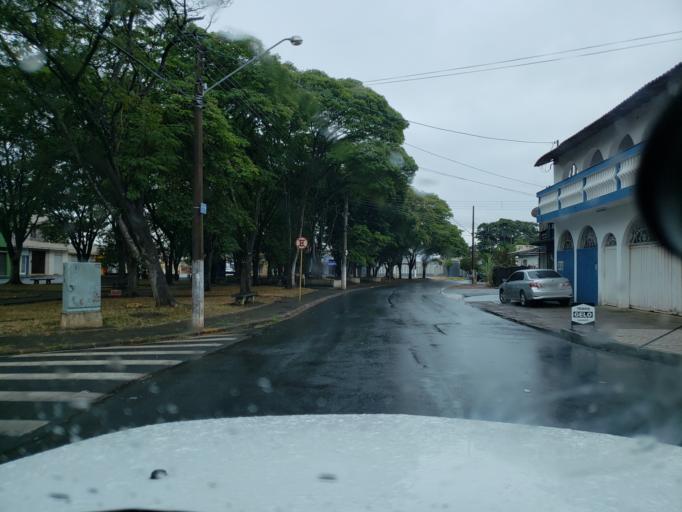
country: BR
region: Sao Paulo
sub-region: Moji-Guacu
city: Mogi-Gaucu
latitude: -22.3531
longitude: -46.9433
